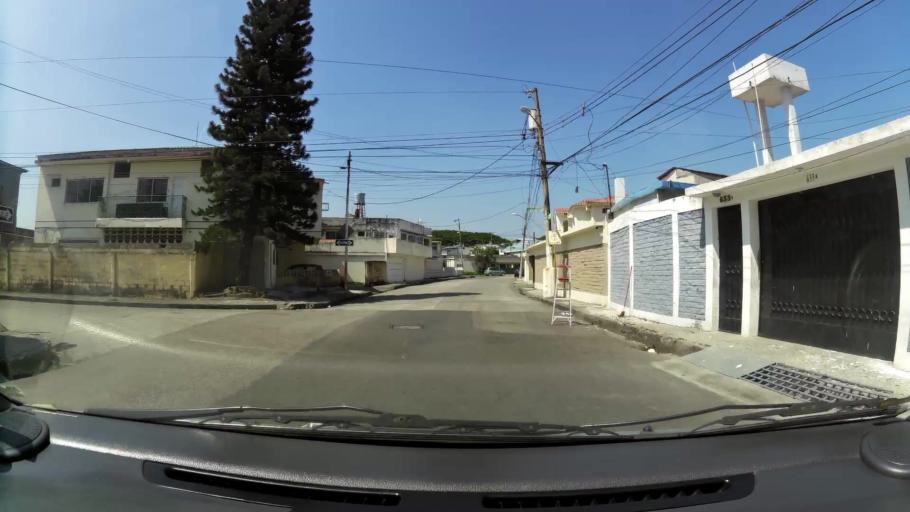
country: EC
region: Guayas
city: Guayaquil
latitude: -2.1698
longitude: -79.9139
